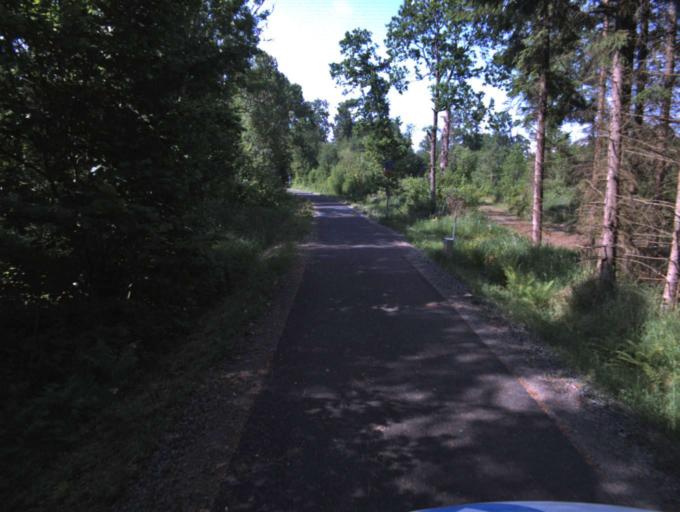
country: SE
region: Skane
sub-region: Kristianstads Kommun
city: Tollarp
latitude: 56.1972
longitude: 14.2891
